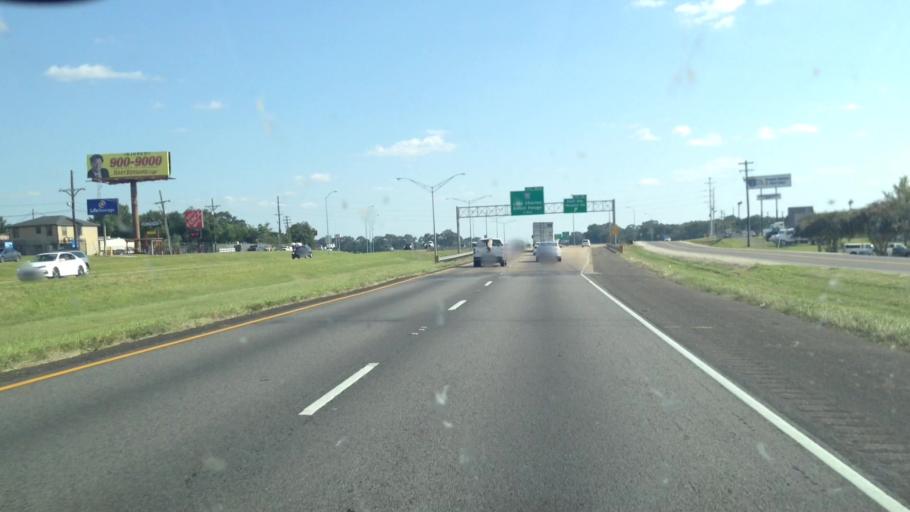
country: US
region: Louisiana
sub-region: Lafayette Parish
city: Carencro
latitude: 30.2794
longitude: -92.0204
